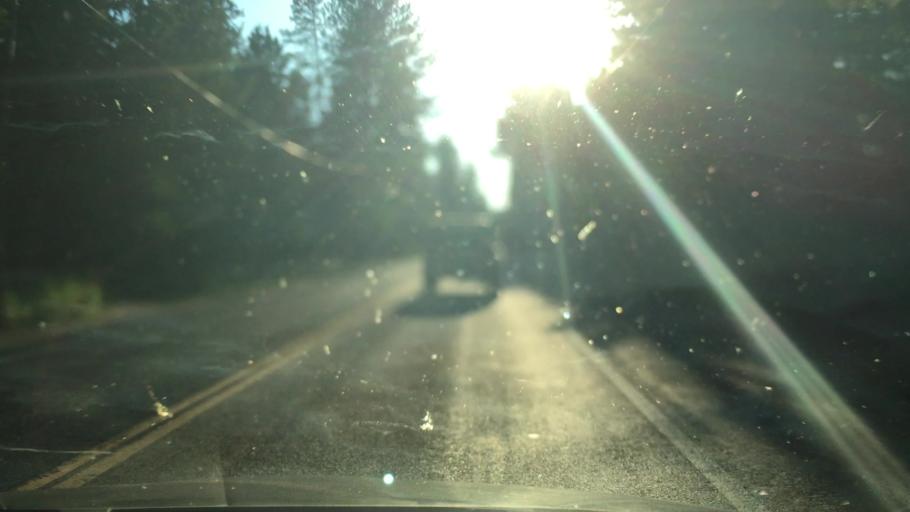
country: US
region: Idaho
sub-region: Valley County
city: McCall
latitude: 44.9106
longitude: -116.1110
